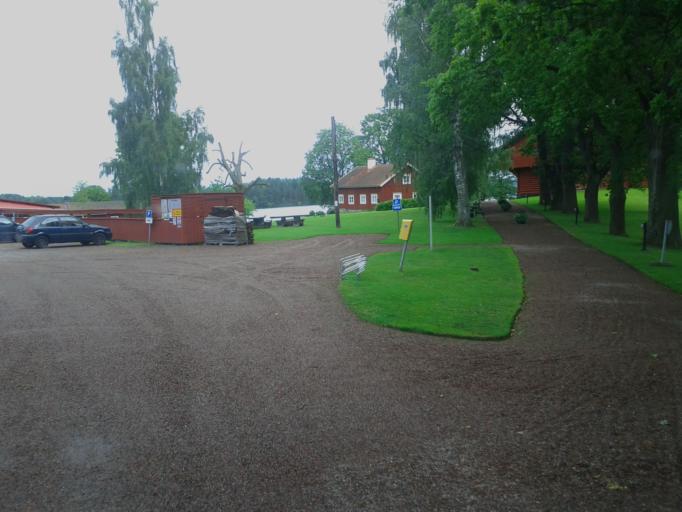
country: SE
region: Dalarna
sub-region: Borlange Kommun
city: Ornas
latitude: 60.5078
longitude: 15.5518
